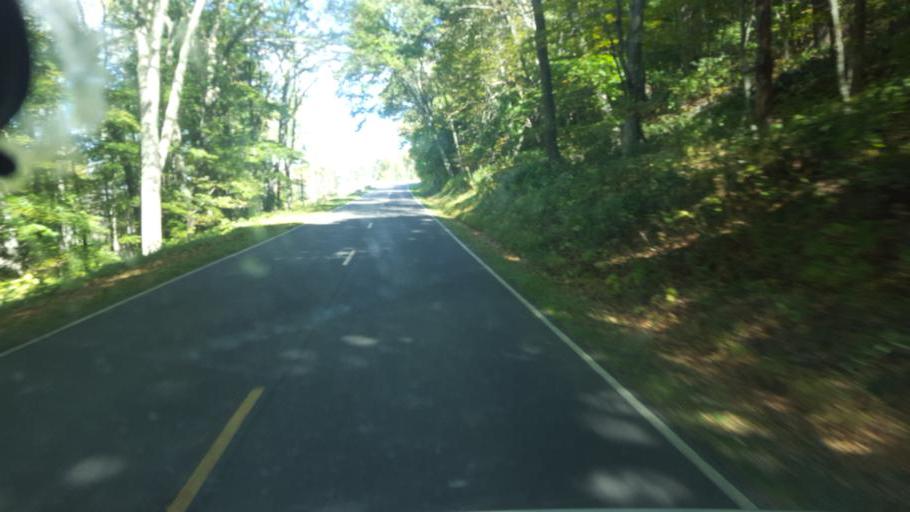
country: US
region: Virginia
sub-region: Page County
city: Stanley
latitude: 38.4764
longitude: -78.4566
